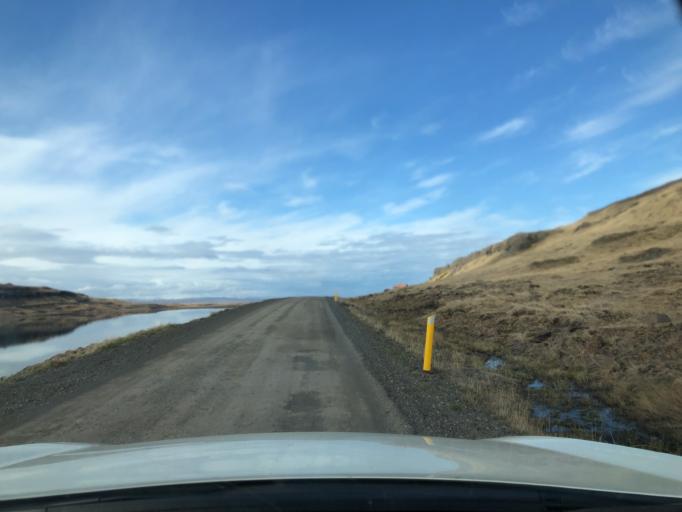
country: IS
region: West
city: Borgarnes
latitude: 65.0565
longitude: -21.6316
